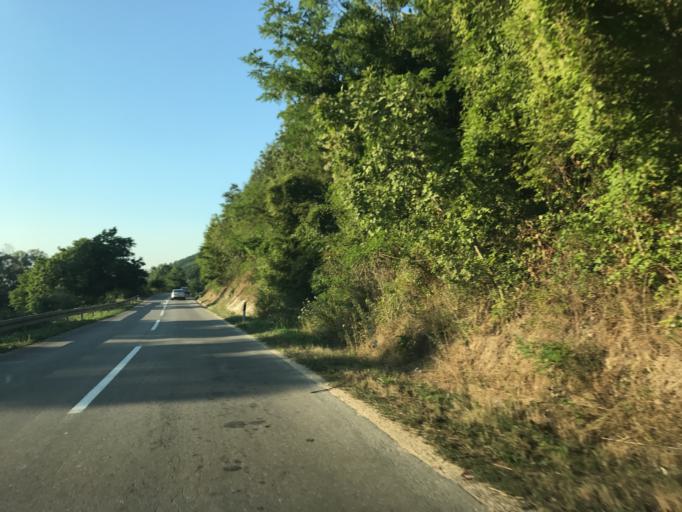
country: RO
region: Mehedinti
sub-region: Comuna Svinita
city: Svinita
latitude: 44.3866
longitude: 22.1756
